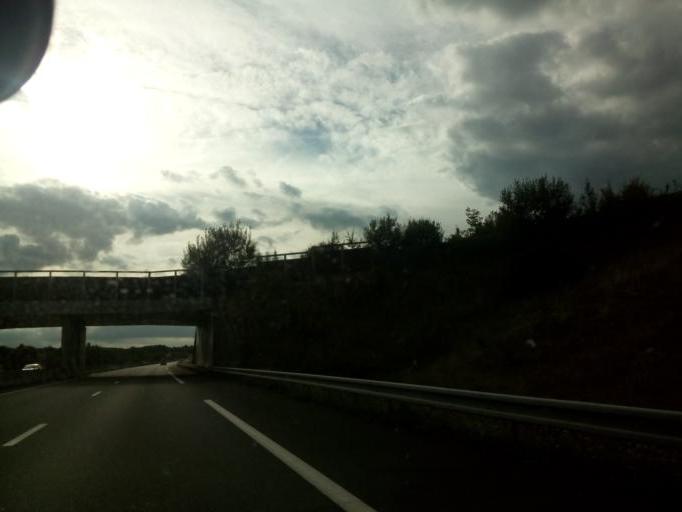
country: FR
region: Centre
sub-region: Departement du Loir-et-Cher
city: Thesee
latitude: 47.2919
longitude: 1.2904
